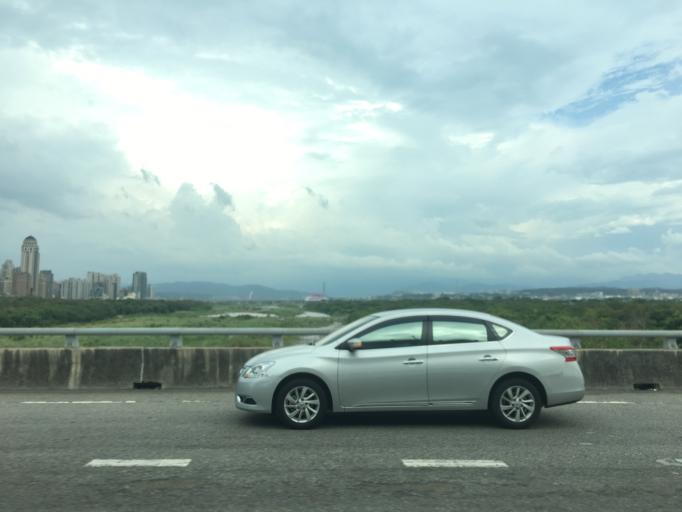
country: TW
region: Taiwan
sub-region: Hsinchu
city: Zhubei
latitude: 24.8068
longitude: 121.0184
